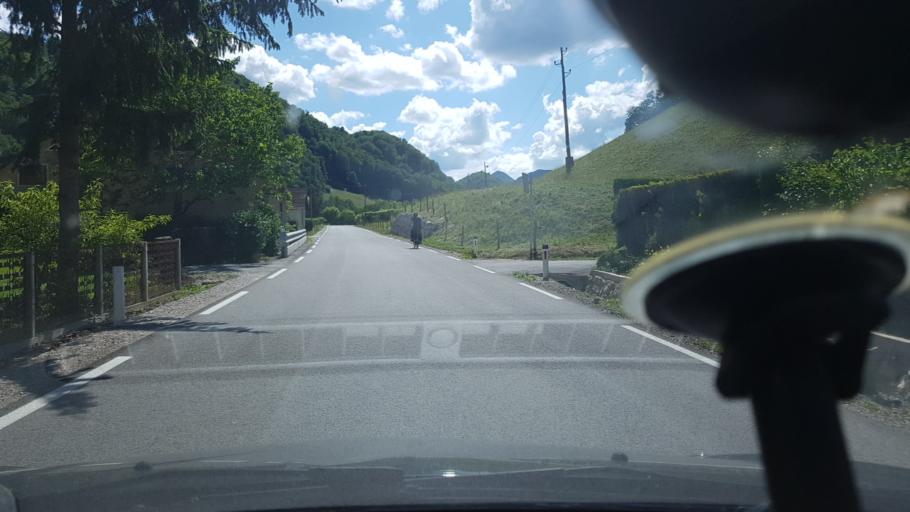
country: SI
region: Zetale
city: Zetale
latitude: 46.2894
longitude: 15.8364
